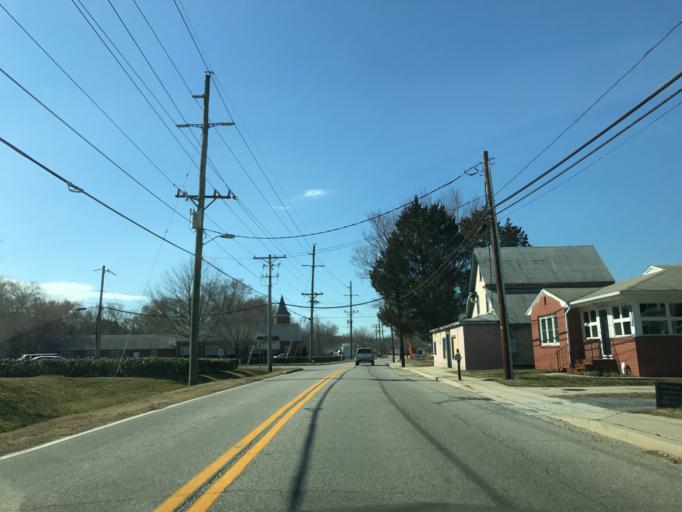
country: US
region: Maryland
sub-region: Queen Anne's County
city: Grasonville
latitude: 38.9591
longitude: -76.2021
